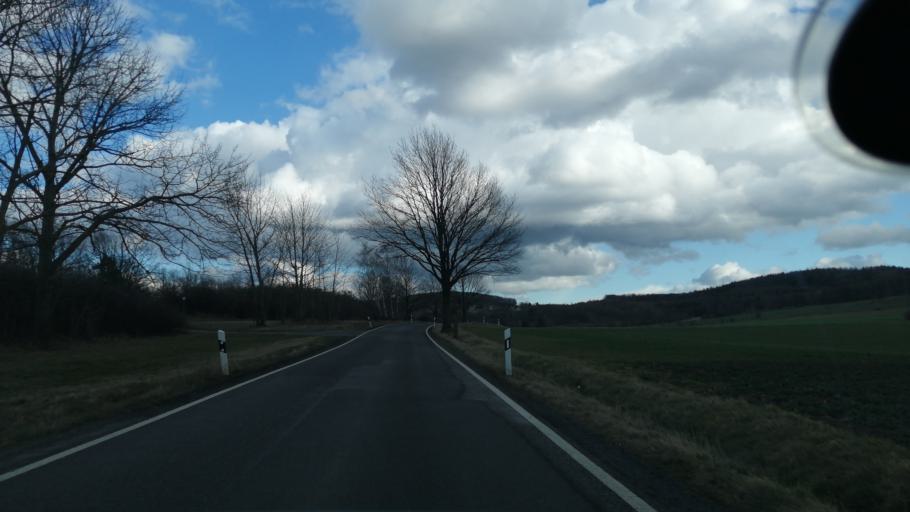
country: DE
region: Saxony
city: Grosspostwitz
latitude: 51.1415
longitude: 14.4498
